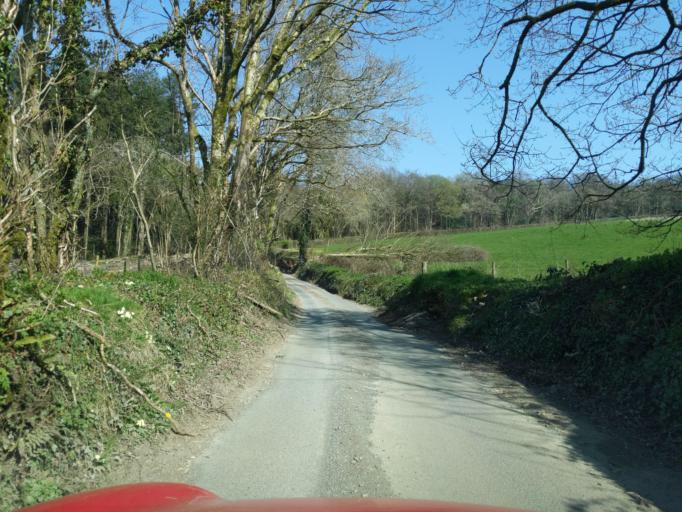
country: GB
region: England
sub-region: Devon
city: Bere Alston
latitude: 50.4611
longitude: -4.1410
